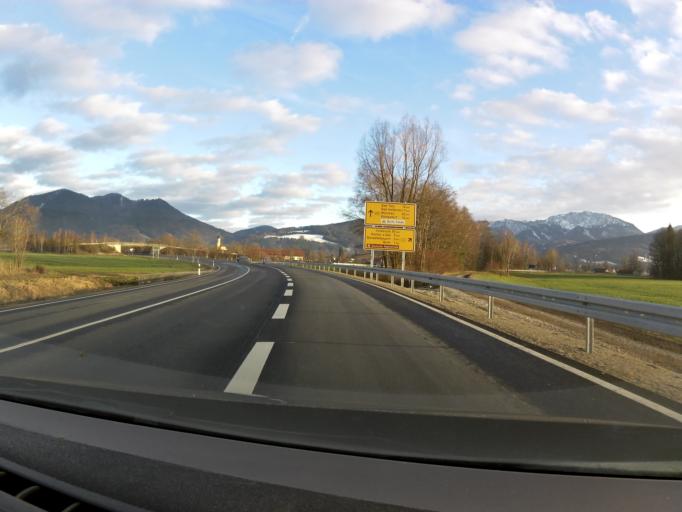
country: DE
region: Bavaria
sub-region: Upper Bavaria
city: Bichl
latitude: 47.7219
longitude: 11.3978
